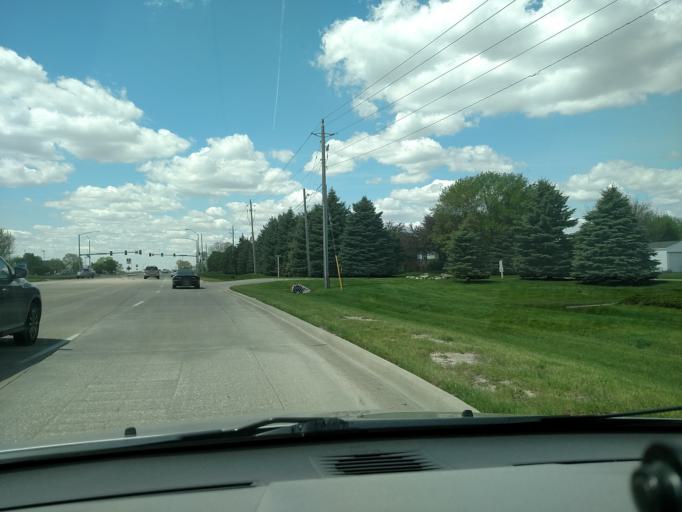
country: US
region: Iowa
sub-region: Polk County
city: Ankeny
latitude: 41.7029
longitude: -93.5918
